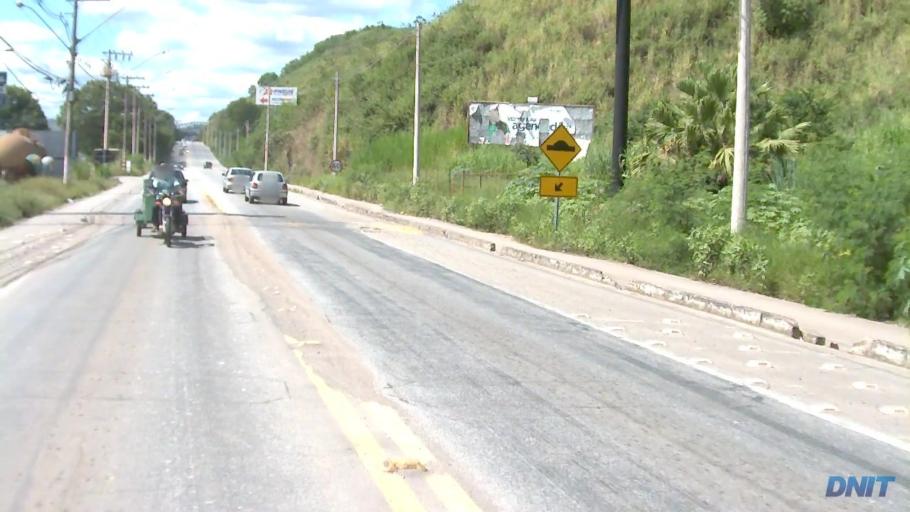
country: BR
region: Minas Gerais
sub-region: Coronel Fabriciano
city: Coronel Fabriciano
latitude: -19.5295
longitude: -42.6604
